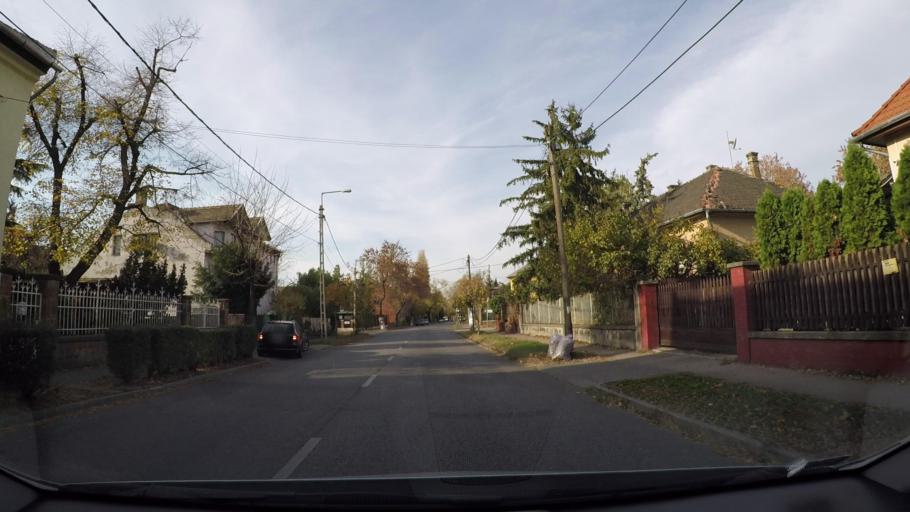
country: HU
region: Budapest
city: Budapest X. keruelet
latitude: 47.4771
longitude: 19.1455
